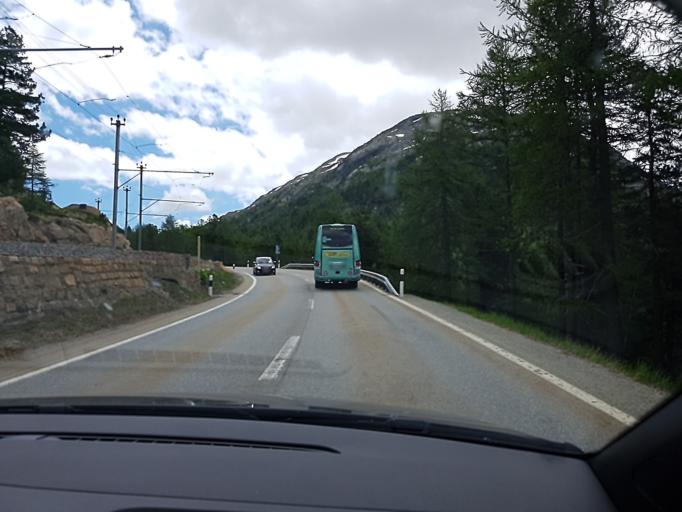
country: CH
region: Grisons
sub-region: Maloja District
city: Pontresina
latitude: 46.4542
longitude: 9.9463
